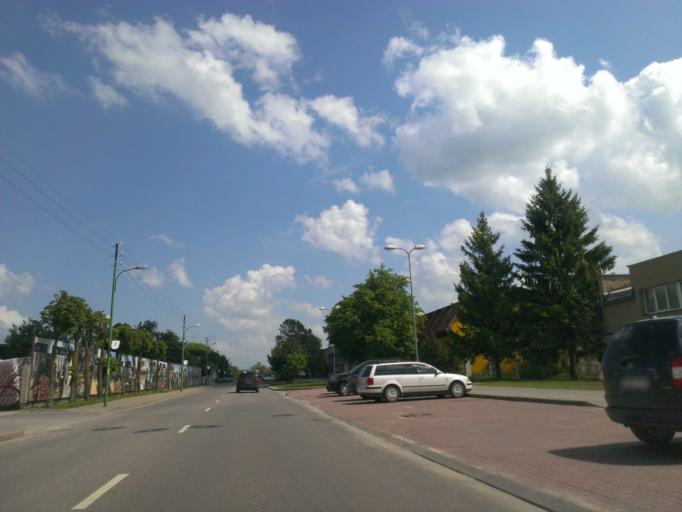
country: LT
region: Klaipedos apskritis
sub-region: Klaipeda
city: Palanga
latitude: 55.9211
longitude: 21.0747
